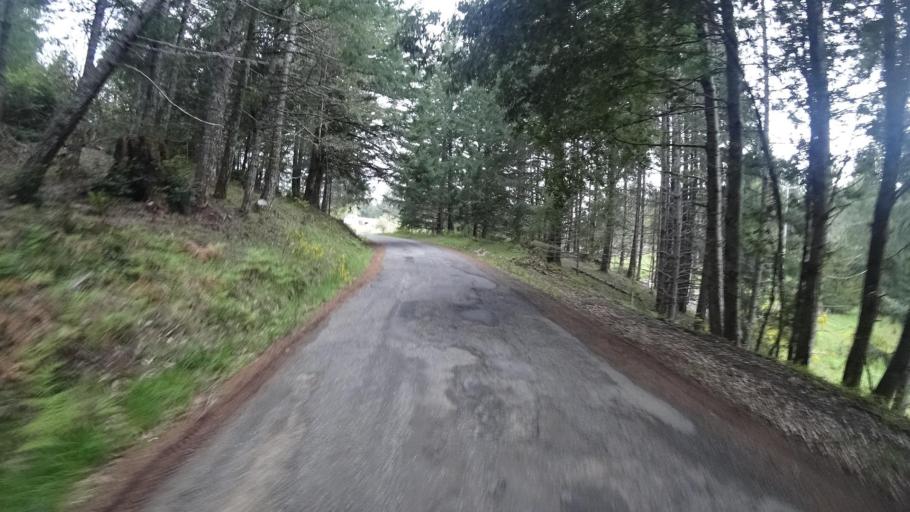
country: US
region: California
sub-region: Humboldt County
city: Redway
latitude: 40.2318
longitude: -123.7609
